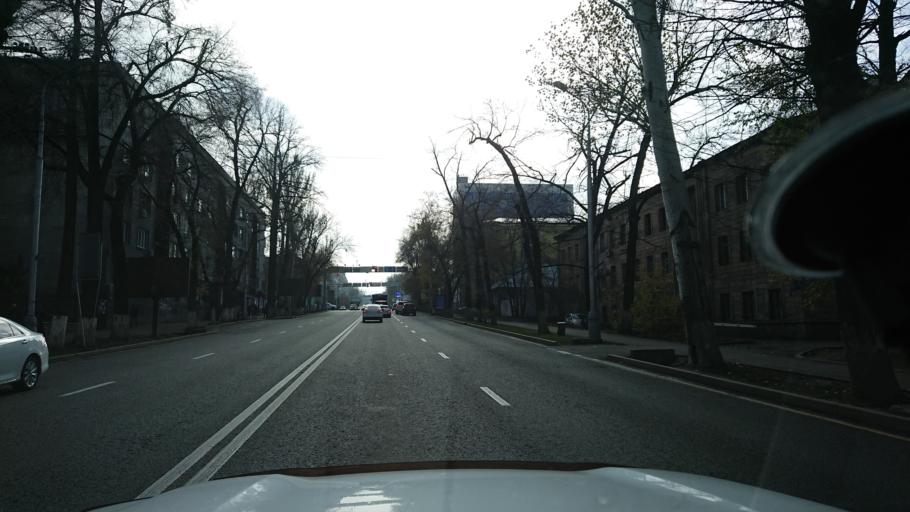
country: KZ
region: Almaty Qalasy
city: Almaty
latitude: 43.2439
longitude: 76.9481
